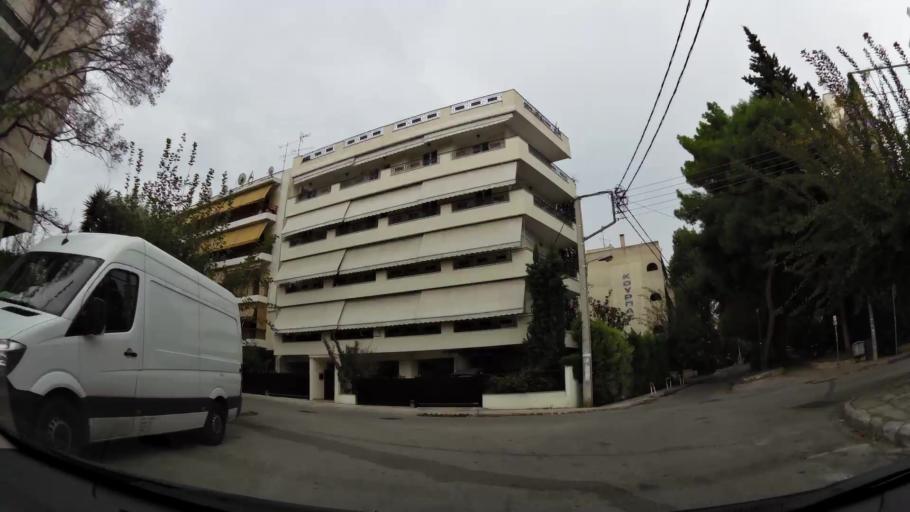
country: GR
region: Attica
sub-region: Nomarchia Athinas
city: Chaidari
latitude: 38.0086
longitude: 23.6684
